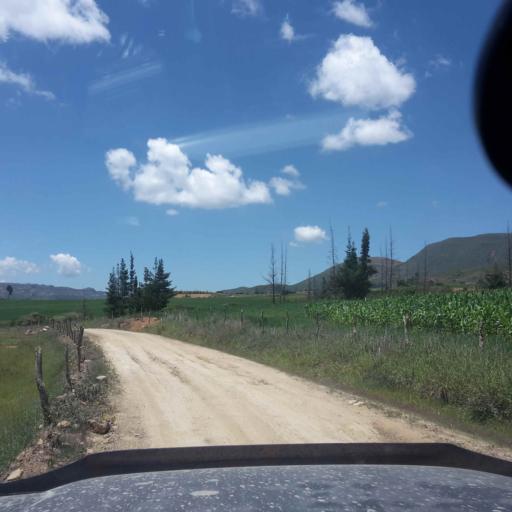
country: BO
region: Cochabamba
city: Totora
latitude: -17.7754
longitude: -65.2566
